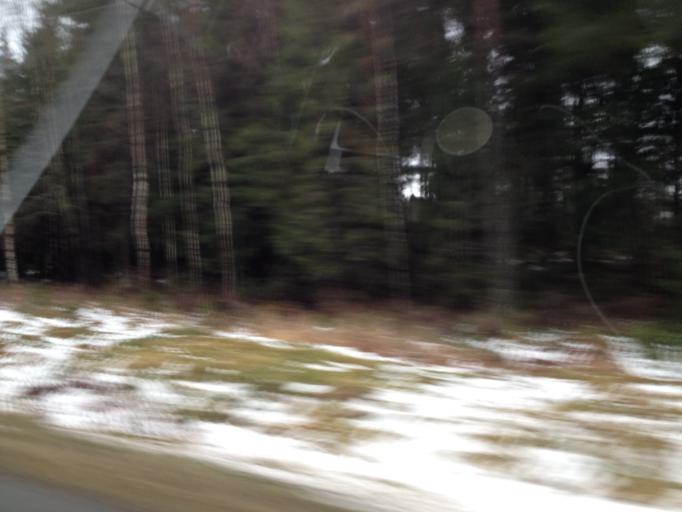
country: FI
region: Uusimaa
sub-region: Raaseporin
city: Ekenaes
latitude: 59.9637
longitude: 23.3748
